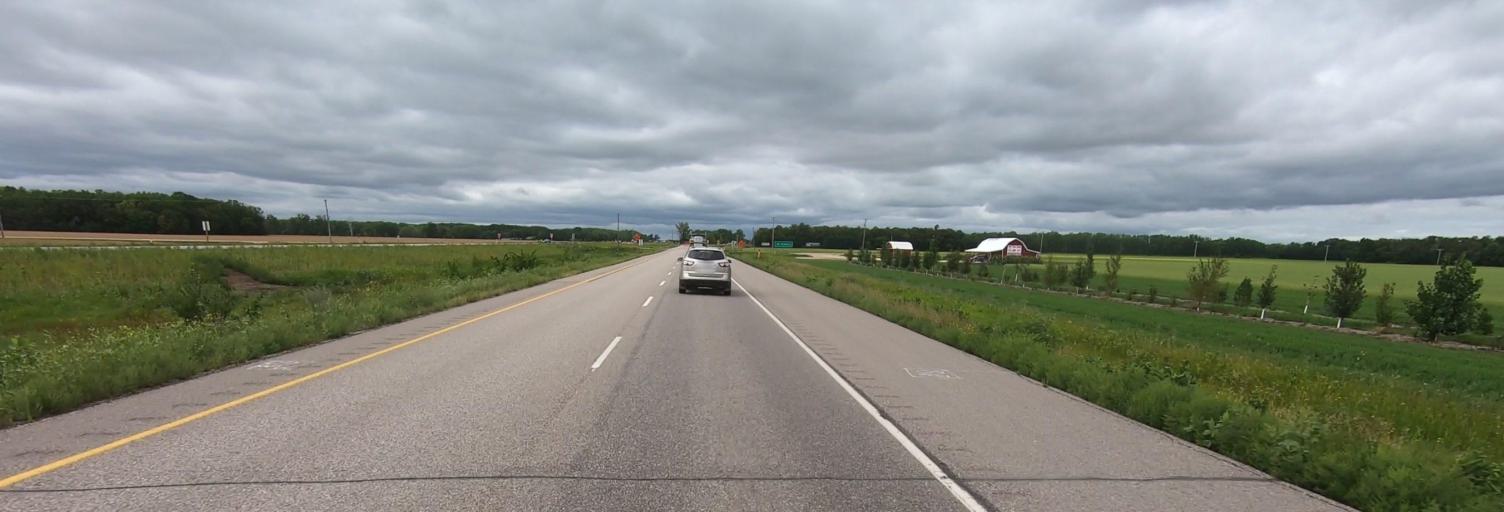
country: CA
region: Manitoba
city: Portage la Prairie
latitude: 49.9657
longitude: -98.0753
